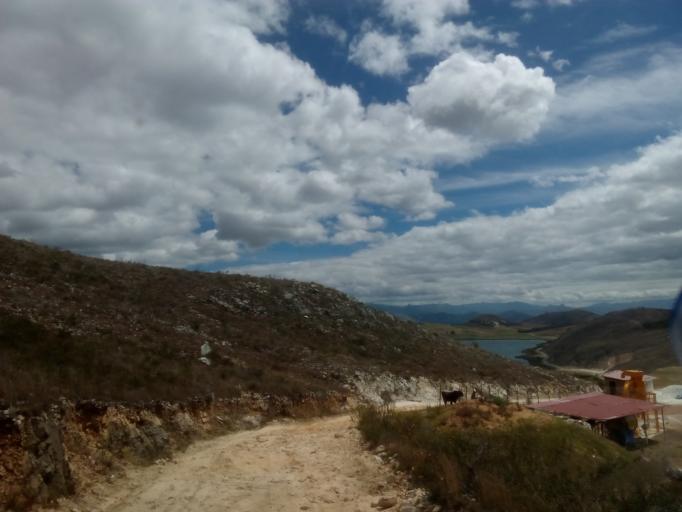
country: PE
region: La Libertad
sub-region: Sanchez Carrion
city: Curgos
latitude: -7.8004
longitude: -77.9751
